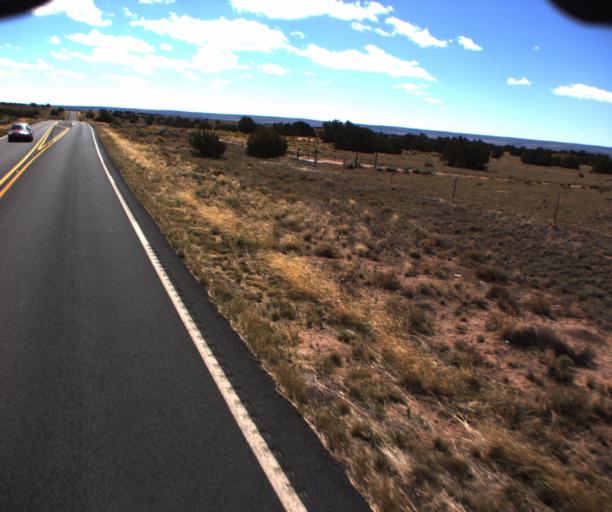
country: US
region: Arizona
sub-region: Apache County
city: Houck
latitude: 35.1259
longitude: -109.3274
